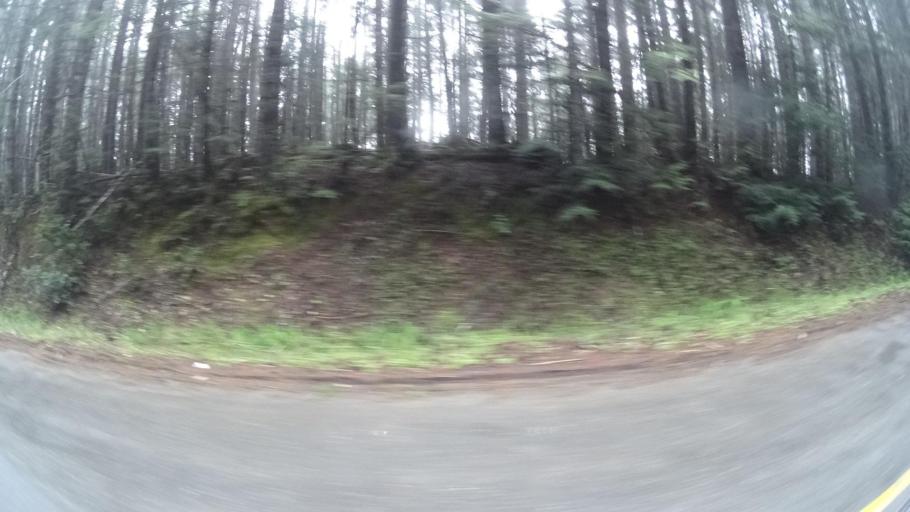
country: US
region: California
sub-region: Humboldt County
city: Westhaven-Moonstone
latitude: 41.2498
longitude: -123.9848
